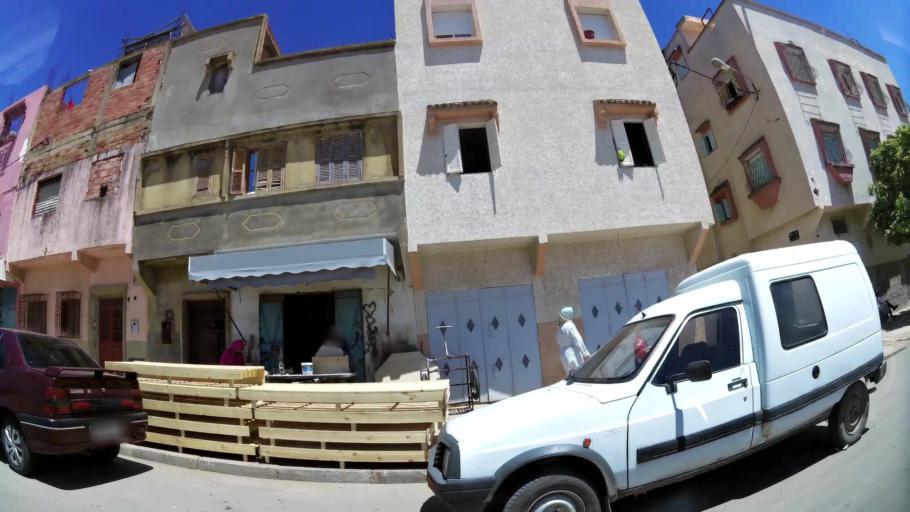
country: MA
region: Meknes-Tafilalet
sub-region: Meknes
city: Meknes
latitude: 33.9062
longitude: -5.5801
